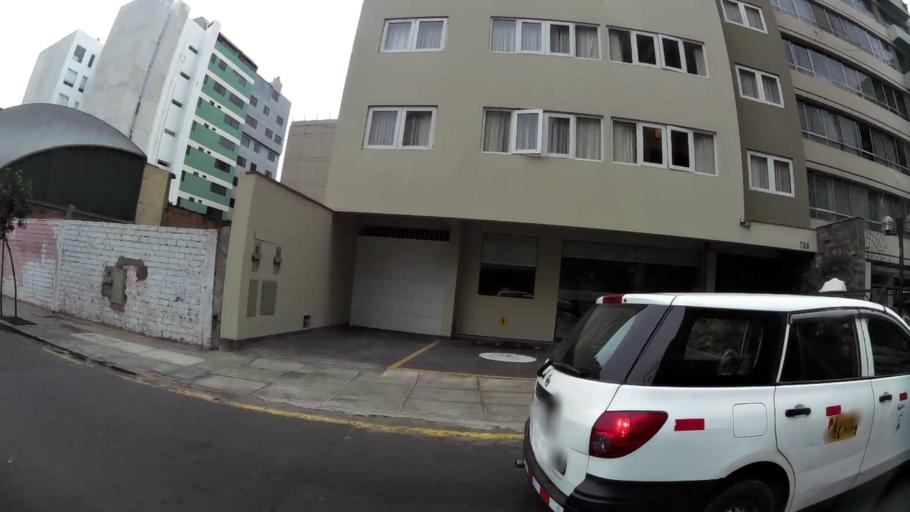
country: PE
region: Lima
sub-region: Lima
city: San Isidro
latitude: -12.1253
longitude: -77.0270
